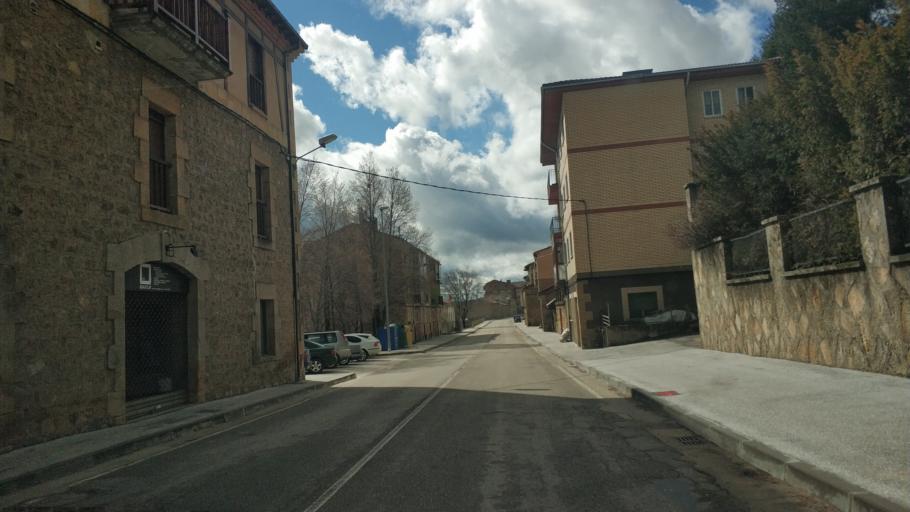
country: ES
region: Castille and Leon
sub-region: Provincia de Burgos
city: Quintanar de la Sierra
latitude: 41.9849
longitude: -3.0333
